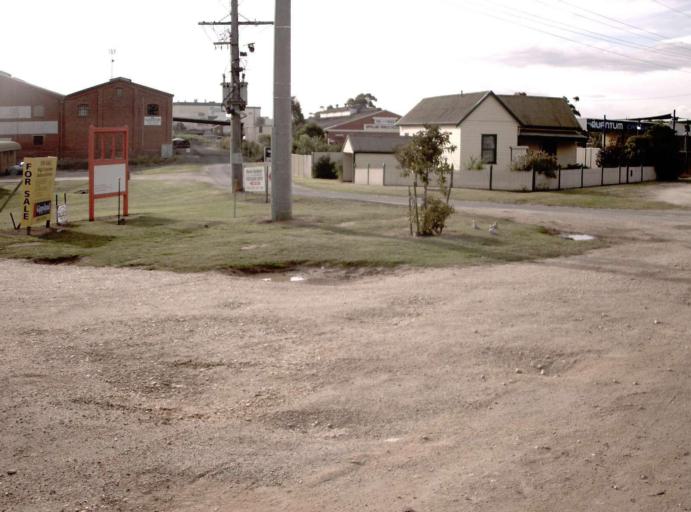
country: AU
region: Victoria
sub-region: Wellington
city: Sale
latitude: -37.9736
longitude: 146.9852
